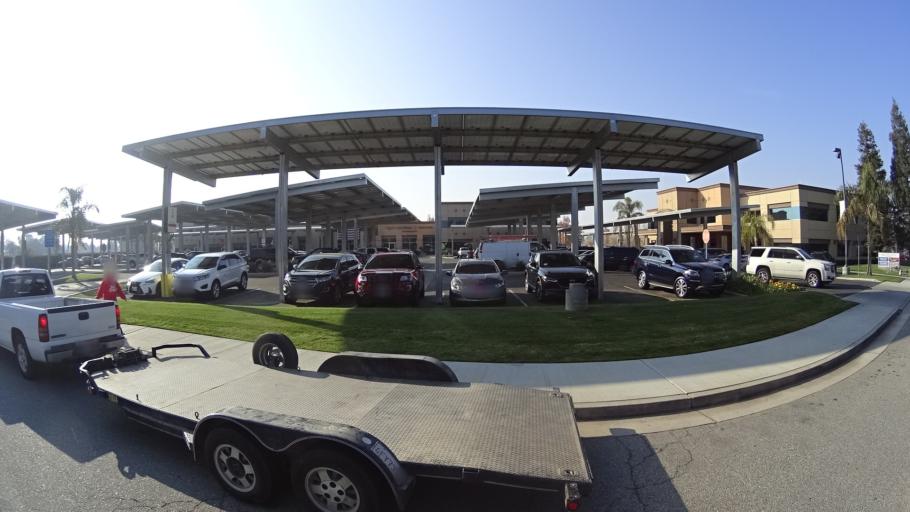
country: US
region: California
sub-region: Kern County
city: Greenacres
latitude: 35.3616
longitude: -119.0732
